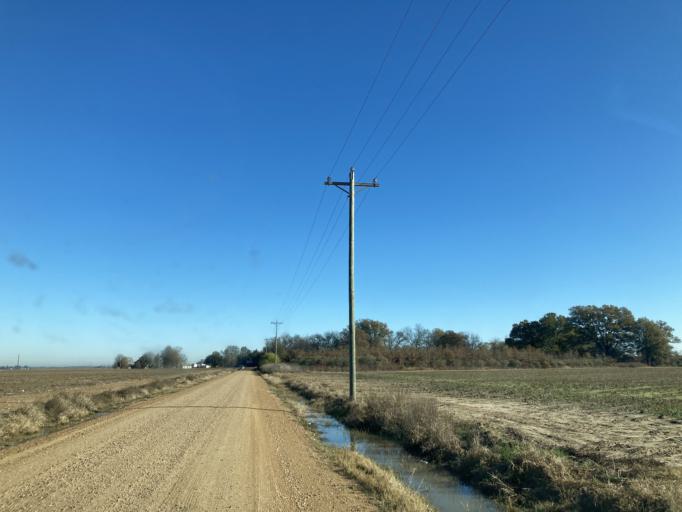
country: US
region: Mississippi
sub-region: Yazoo County
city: Yazoo City
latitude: 32.9245
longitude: -90.5909
